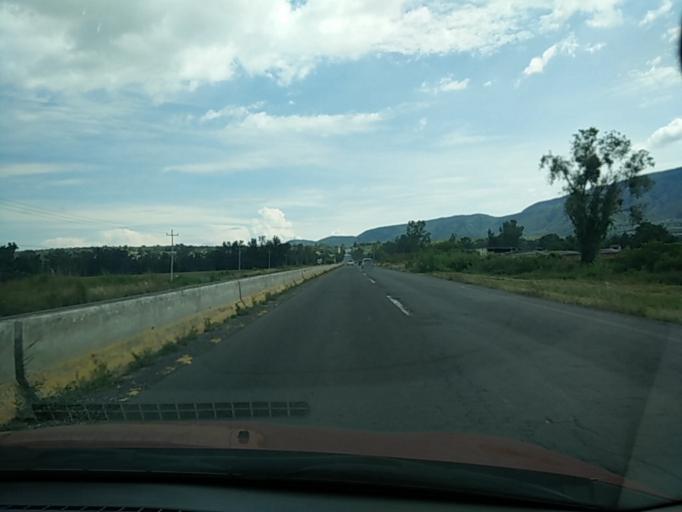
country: MX
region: Jalisco
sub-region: Ixtlahuacan de los Membrillos
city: Los Cedros
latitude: 20.3889
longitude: -103.2218
